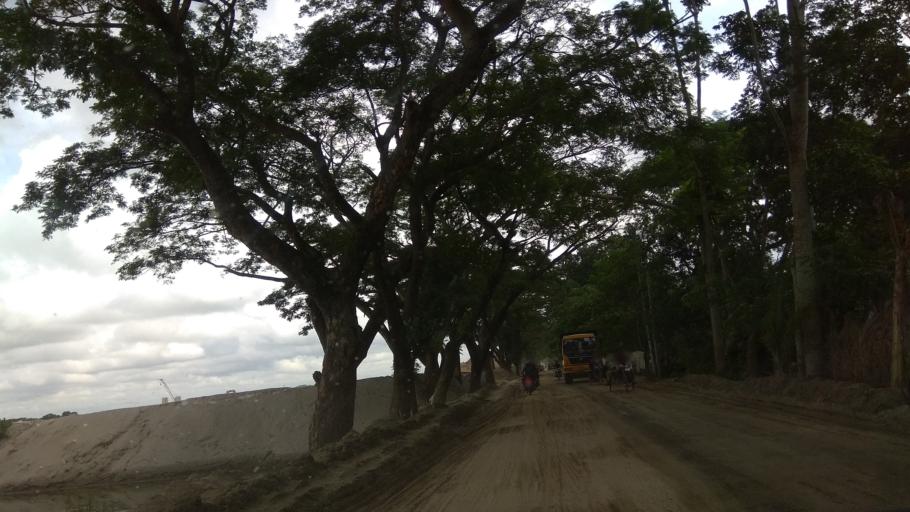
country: BD
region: Khulna
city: Kalia
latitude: 23.1987
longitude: 89.6971
